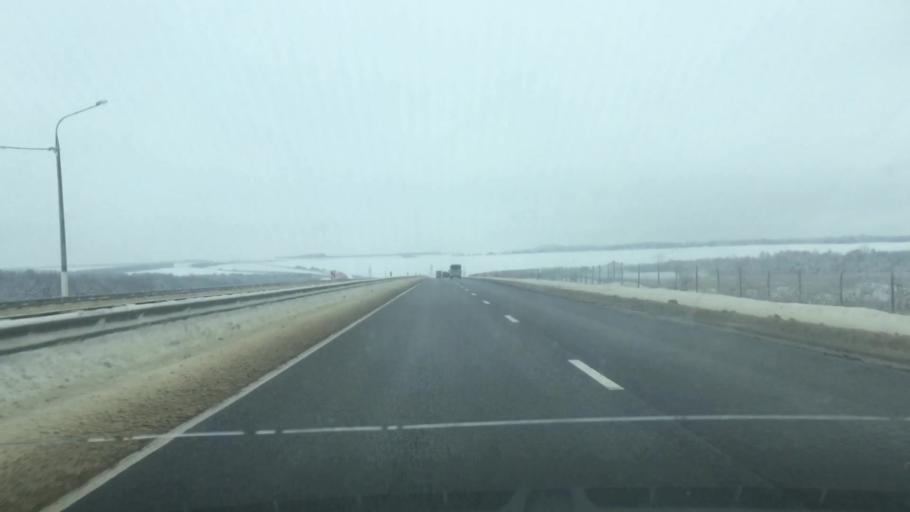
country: RU
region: Tula
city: Kazachka
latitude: 53.2862
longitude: 38.1791
